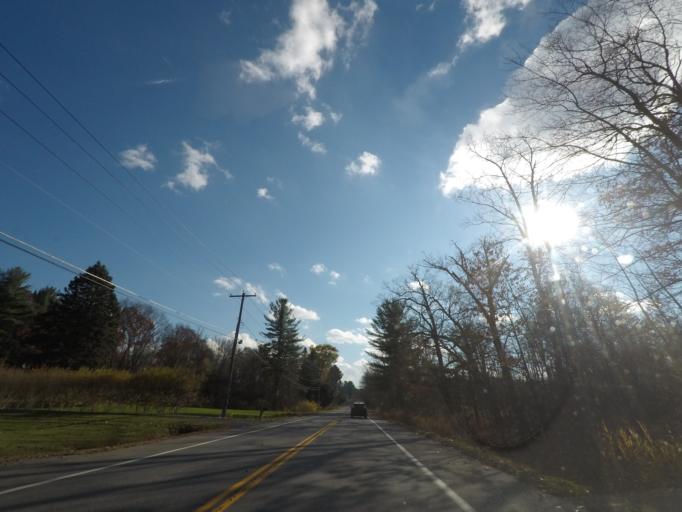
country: US
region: New York
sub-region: Schenectady County
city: East Glenville
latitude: 42.8844
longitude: -73.8878
